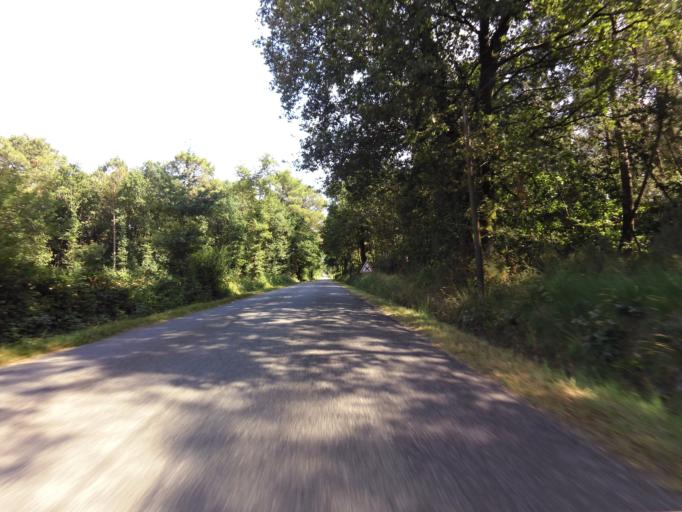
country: FR
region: Brittany
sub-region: Departement du Morbihan
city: Limerzel
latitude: 47.6547
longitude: -2.3898
